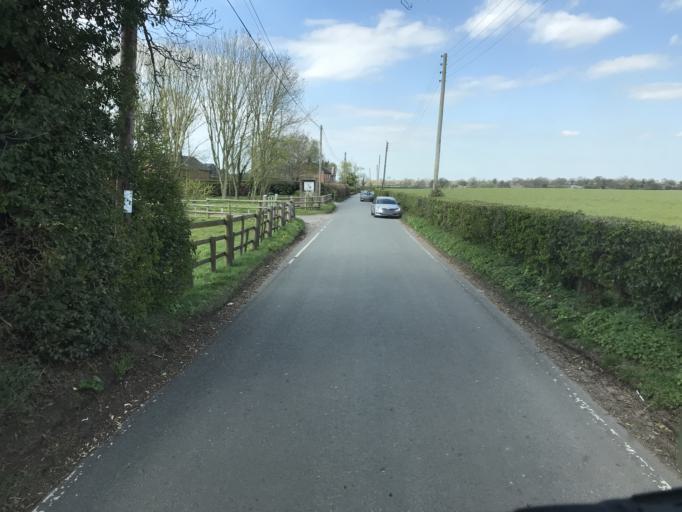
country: GB
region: England
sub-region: Cheshire West and Chester
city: Tarvin
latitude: 53.2085
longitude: -2.7673
